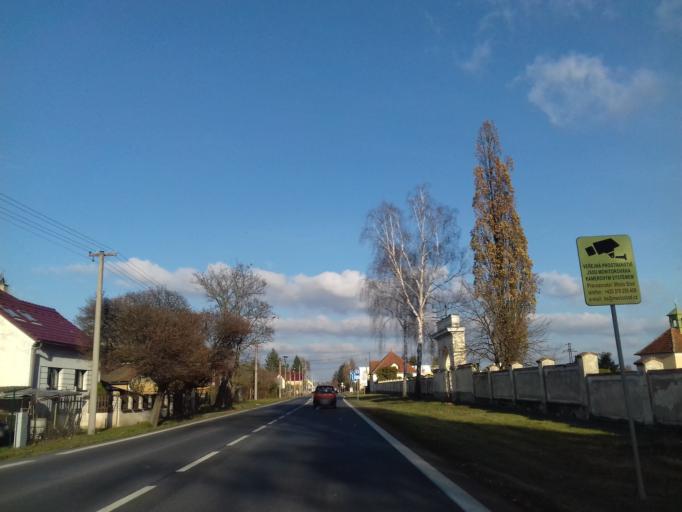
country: CZ
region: Plzensky
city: Stod
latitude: 49.6320
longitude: 13.1590
